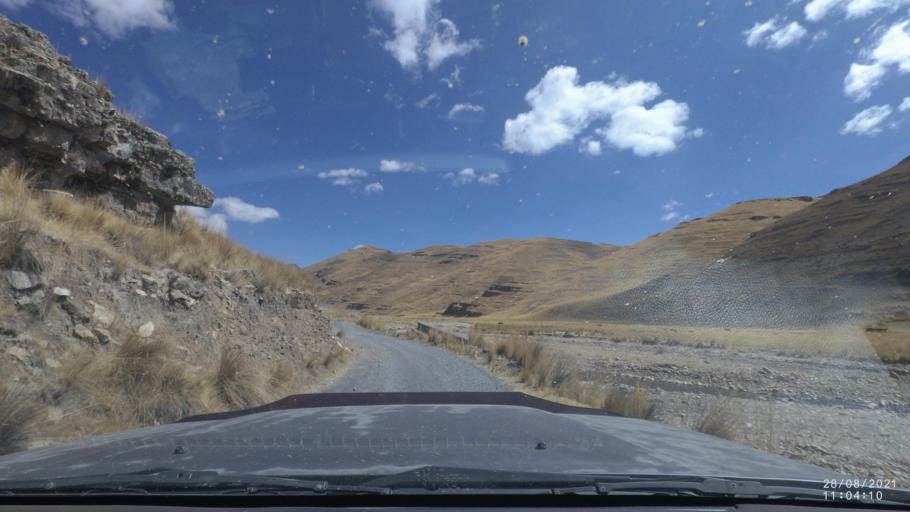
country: BO
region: Cochabamba
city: Cochabamba
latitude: -17.1748
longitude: -66.2812
